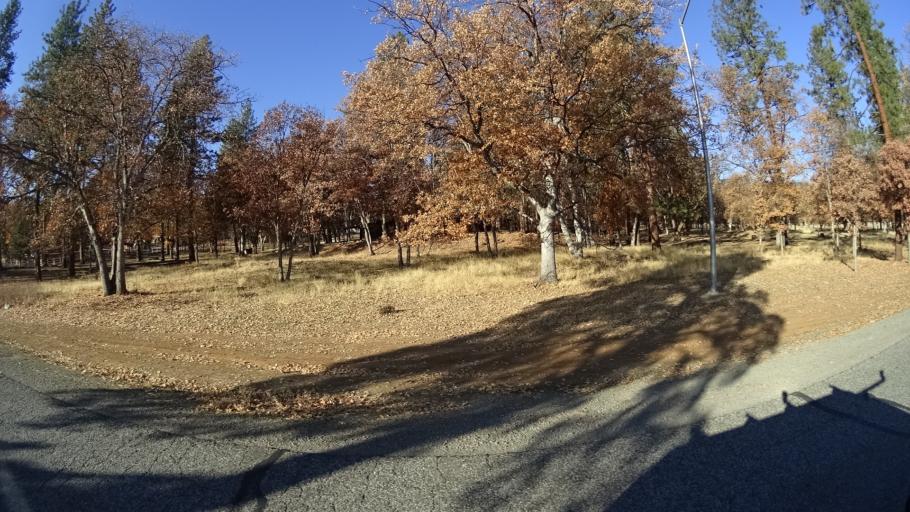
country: US
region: California
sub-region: Siskiyou County
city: Yreka
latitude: 41.7164
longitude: -122.6462
